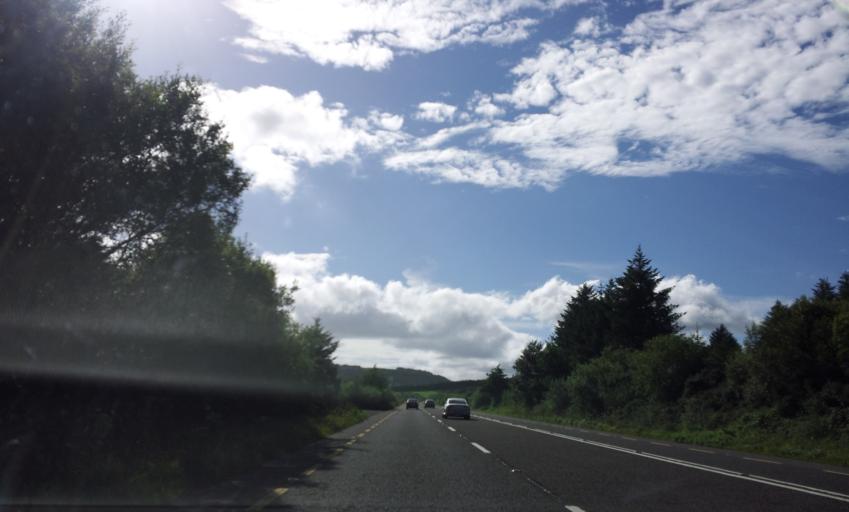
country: IE
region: Munster
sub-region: County Cork
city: Millstreet
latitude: 51.9620
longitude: -9.2194
